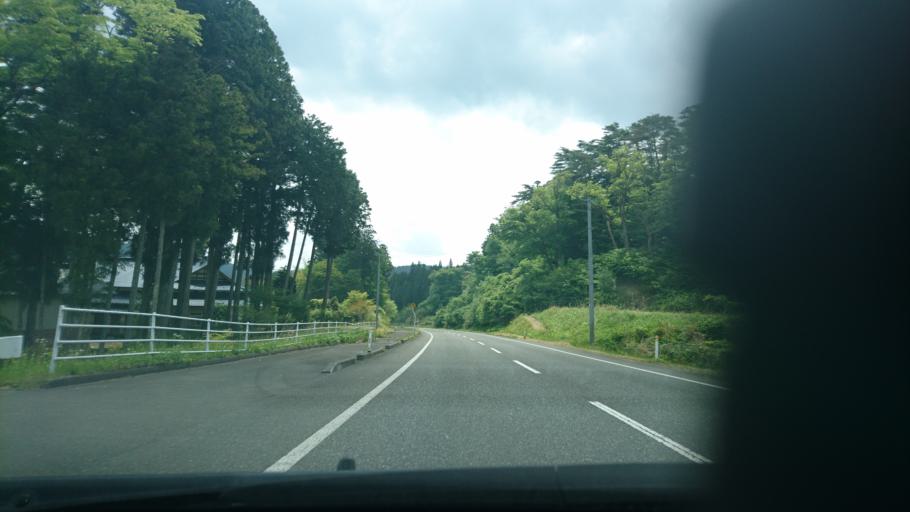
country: JP
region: Iwate
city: Ichinoseki
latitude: 38.8943
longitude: 140.9362
